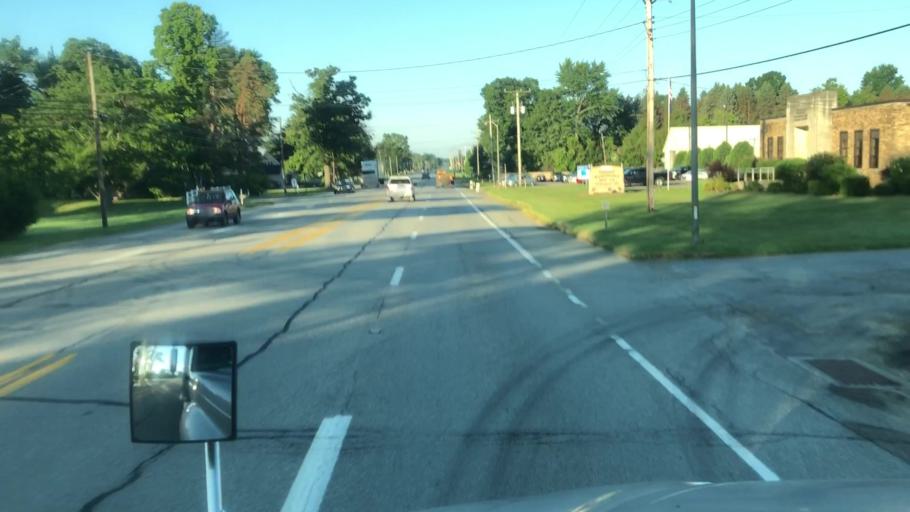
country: US
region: Pennsylvania
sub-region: Venango County
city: Franklin
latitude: 41.3696
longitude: -79.8589
